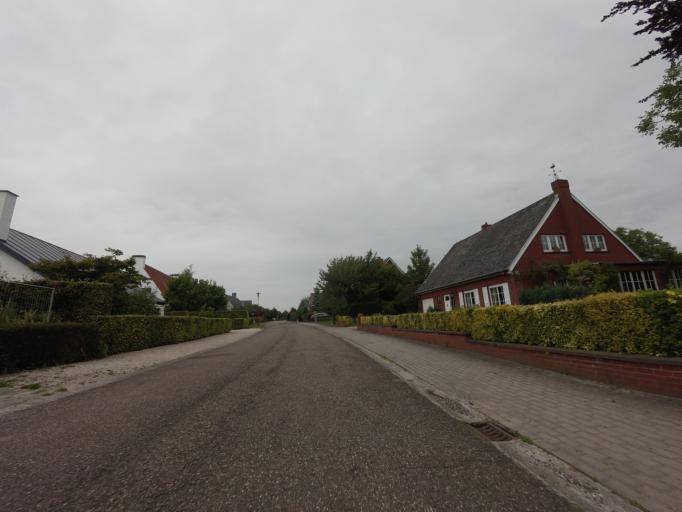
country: BE
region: Flanders
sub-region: Provincie Vlaams-Brabant
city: Grimbergen
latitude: 50.9398
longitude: 4.3689
